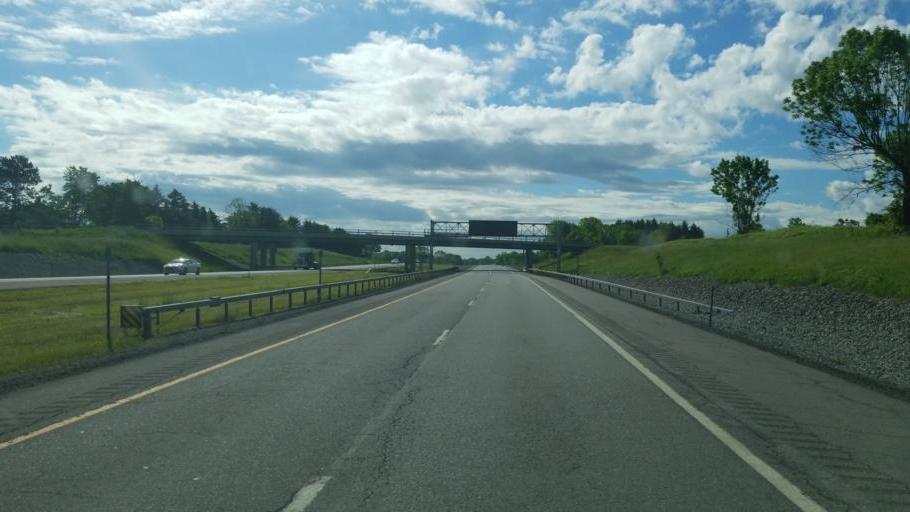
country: US
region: New York
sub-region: Monroe County
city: Pittsford
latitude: 43.0225
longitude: -77.4986
